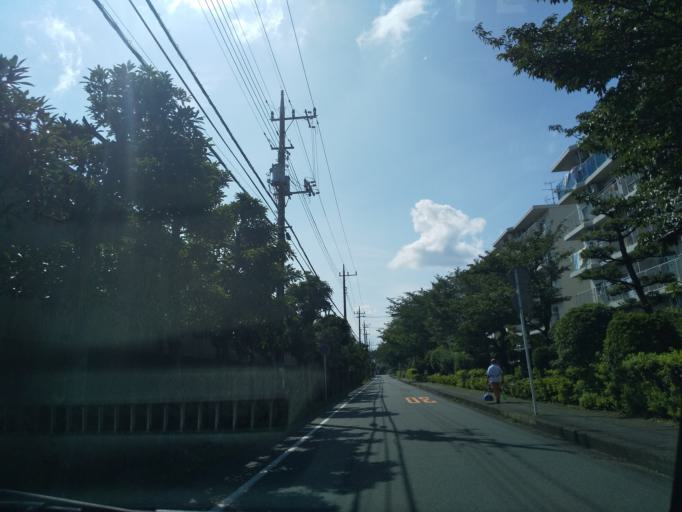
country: JP
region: Kanagawa
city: Zama
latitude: 35.4612
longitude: 139.4131
